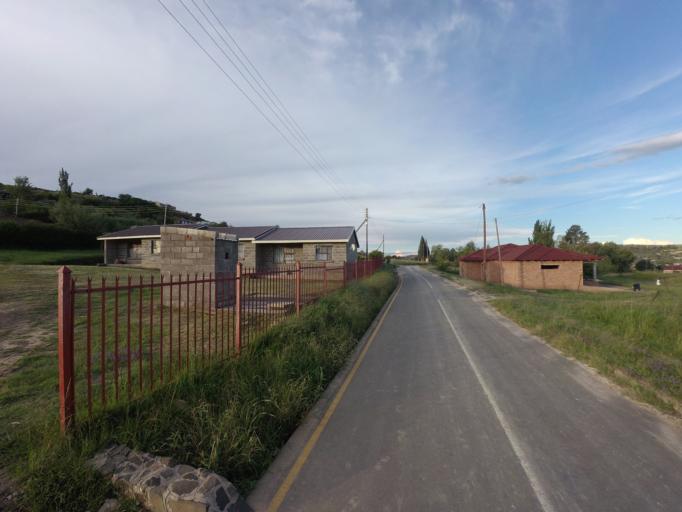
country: LS
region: Maseru
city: Maseru
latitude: -29.3077
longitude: 27.5063
